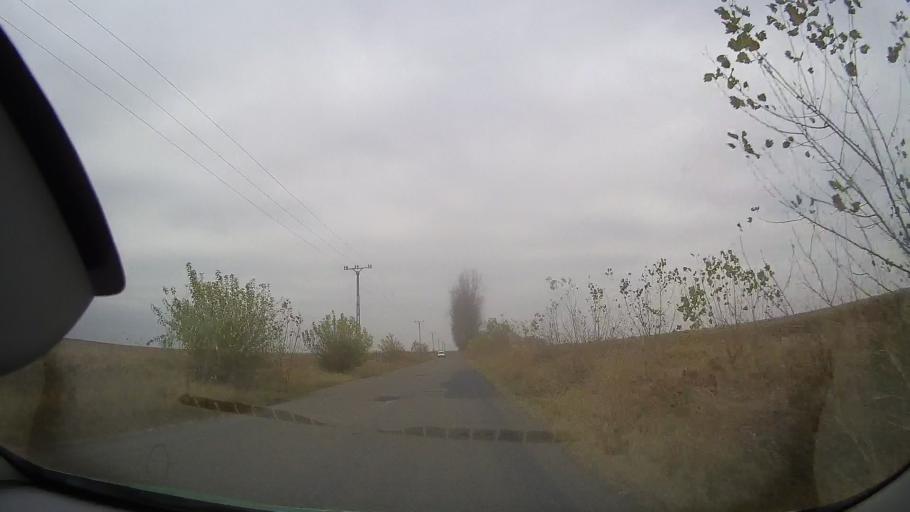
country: RO
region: Buzau
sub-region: Comuna Pogoanele
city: Pogoanele
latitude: 44.9576
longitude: 27.0190
